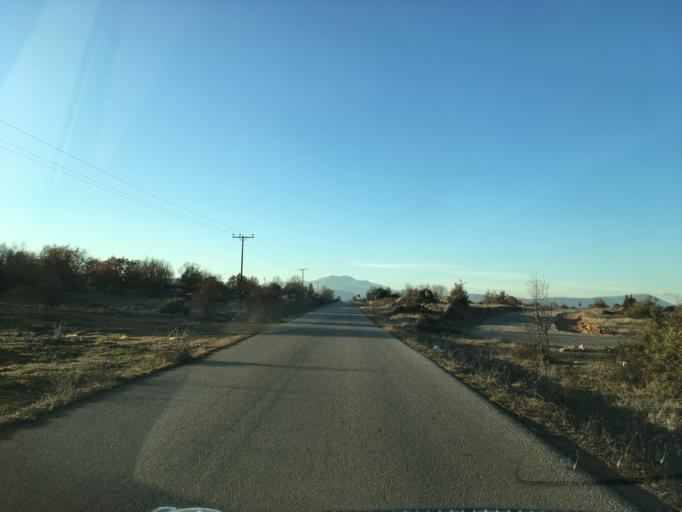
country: GR
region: West Macedonia
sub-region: Nomos Kozanis
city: Kozani
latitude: 40.2697
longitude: 21.7413
